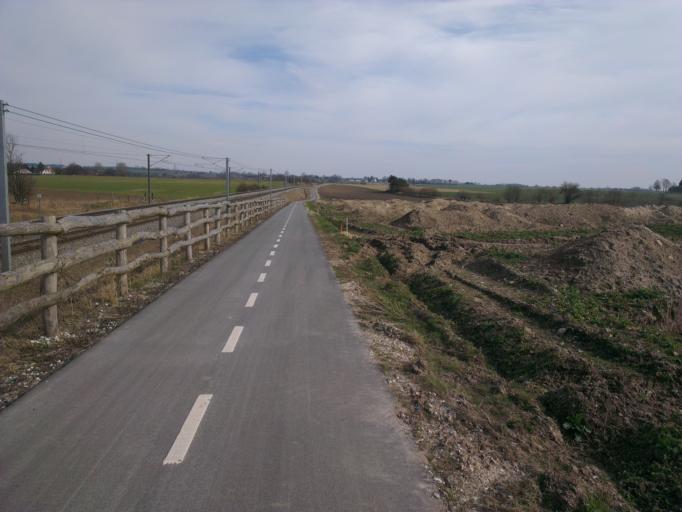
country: DK
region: Capital Region
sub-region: Egedal Kommune
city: Olstykke
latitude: 55.8101
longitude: 12.1168
